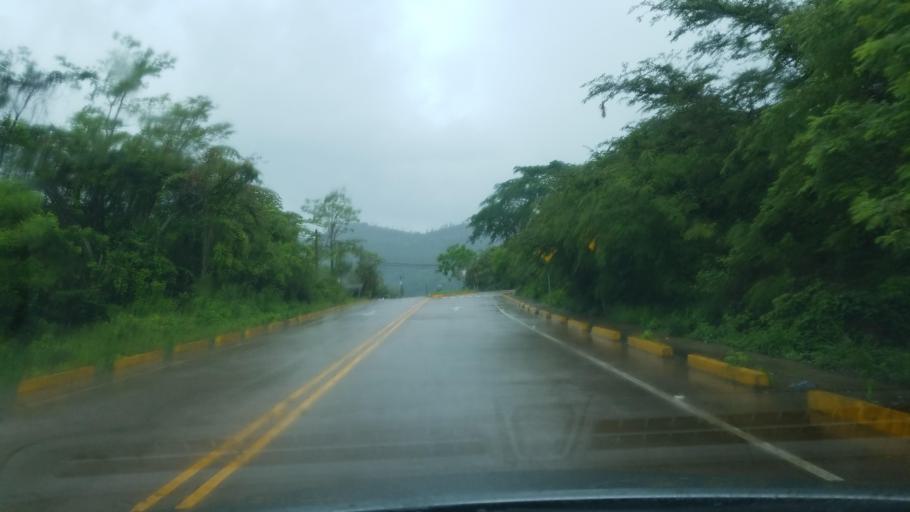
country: HN
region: Copan
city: Copan
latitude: 14.8376
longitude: -89.1614
